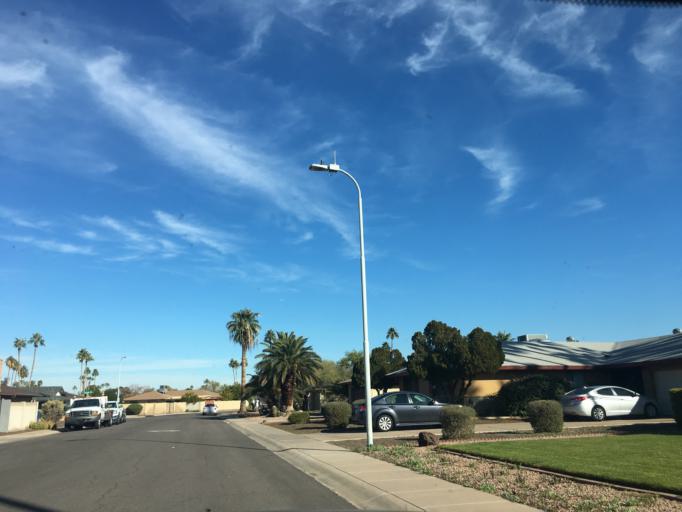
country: US
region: Arizona
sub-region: Maricopa County
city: Tempe
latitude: 33.3867
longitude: -111.9030
